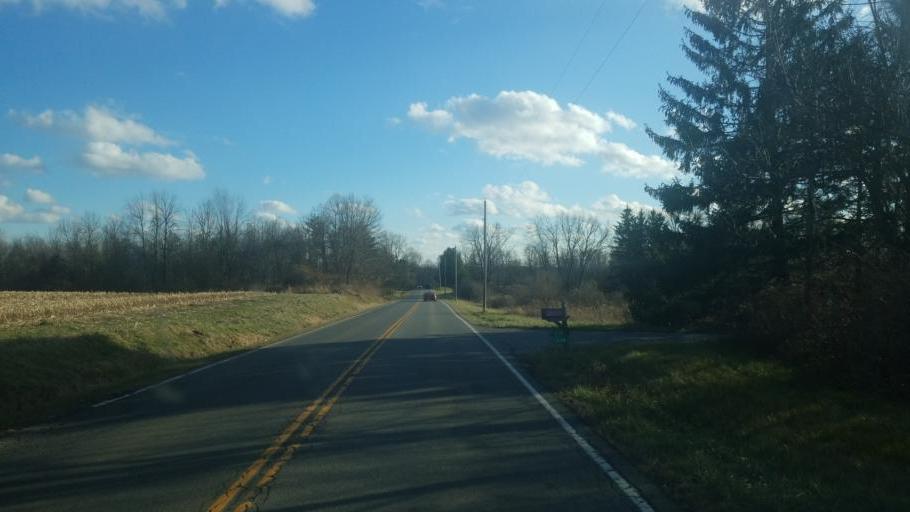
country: US
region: Ohio
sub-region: Richland County
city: Ontario
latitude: 40.7251
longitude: -82.5857
